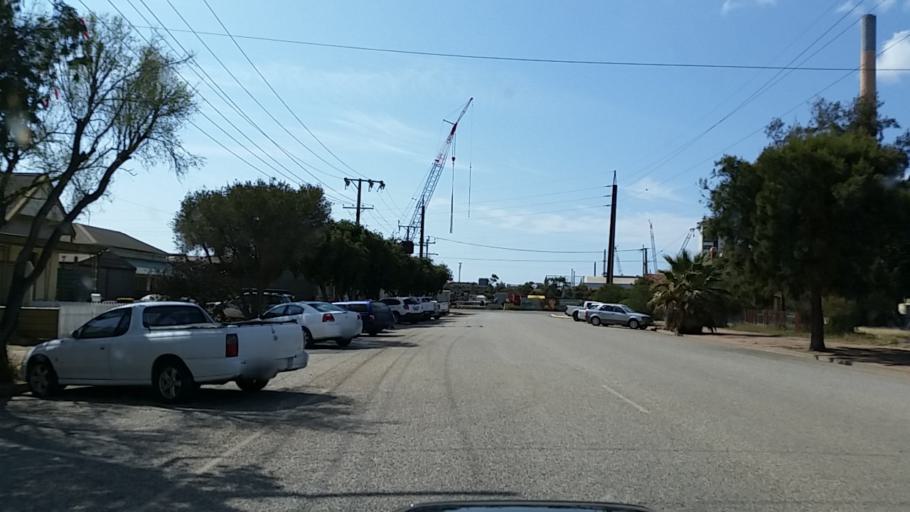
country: AU
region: South Australia
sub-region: Port Pirie City and Dists
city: Port Pirie
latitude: -33.1744
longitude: 138.0083
